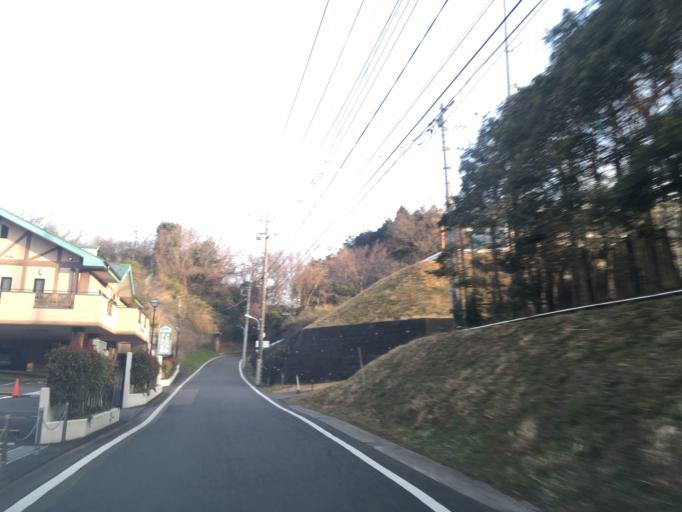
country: JP
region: Tokyo
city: Hino
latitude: 35.6393
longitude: 139.3942
